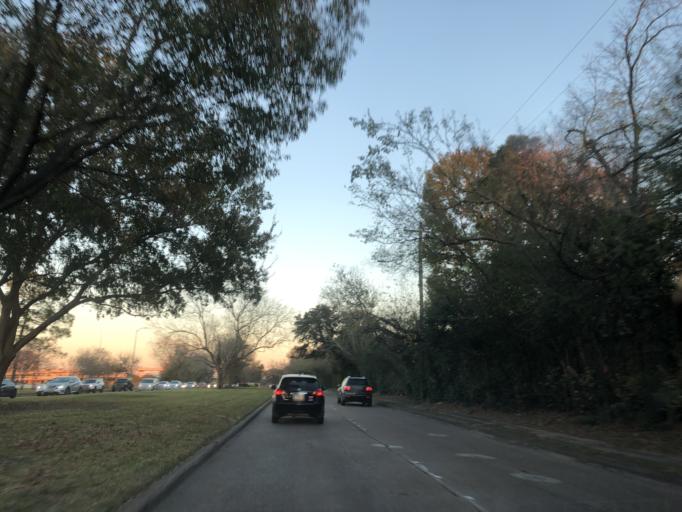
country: US
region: Texas
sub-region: Harris County
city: Bellaire
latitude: 29.6788
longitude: -95.4642
